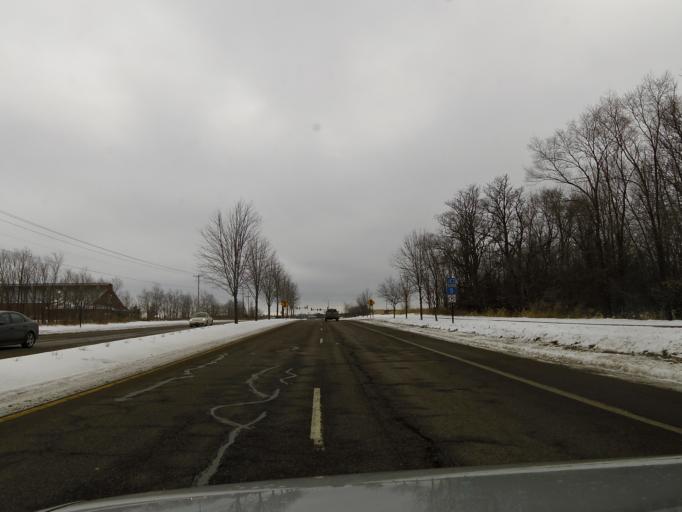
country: US
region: Minnesota
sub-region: Washington County
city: Oakdale
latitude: 45.0004
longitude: -92.9442
